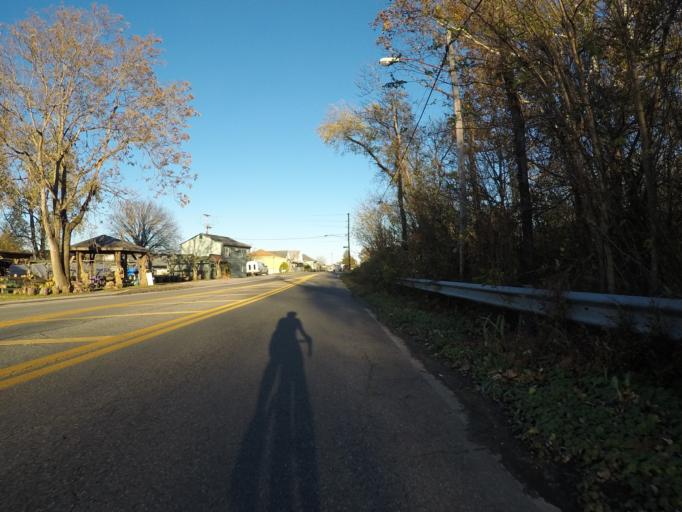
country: US
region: Ohio
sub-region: Lawrence County
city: Burlington
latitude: 38.4058
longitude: -82.4916
